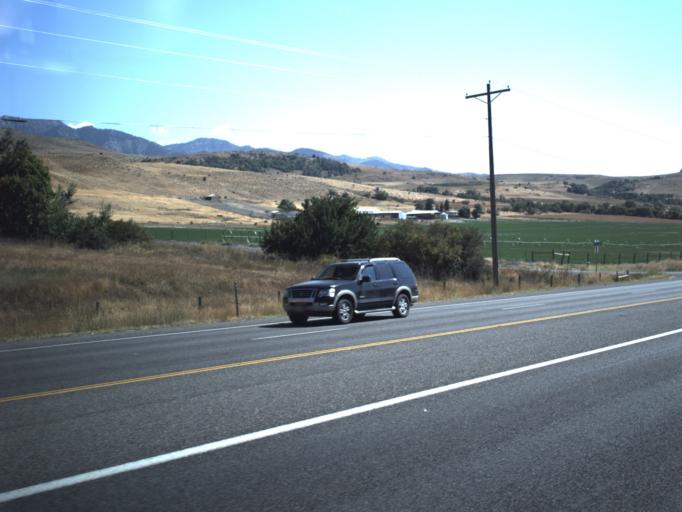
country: US
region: Utah
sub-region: Cache County
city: Richmond
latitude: 41.8966
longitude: -111.8149
